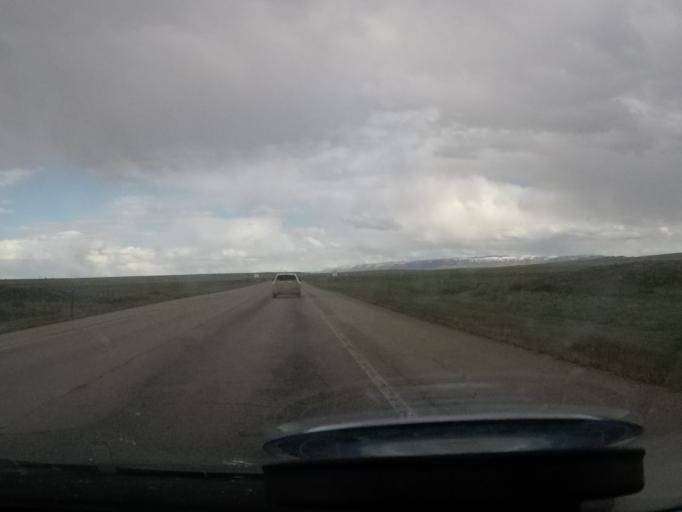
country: US
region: Wyoming
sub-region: Natrona County
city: Mills
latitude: 42.9511
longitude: -106.6353
